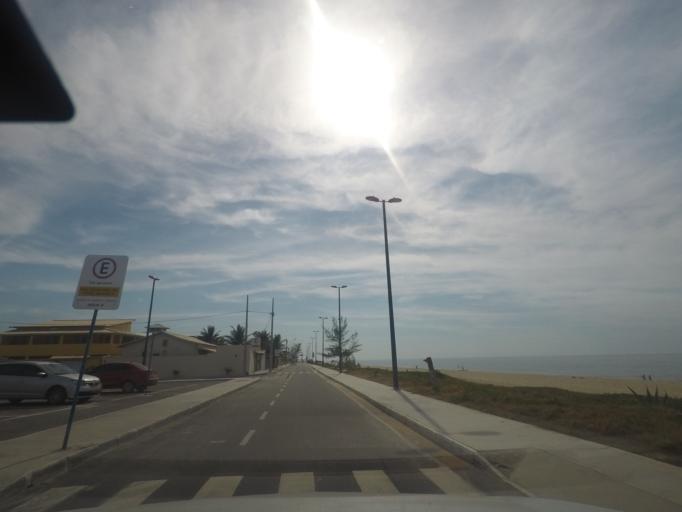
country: BR
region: Rio de Janeiro
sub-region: Marica
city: Marica
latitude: -22.9613
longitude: -42.8223
